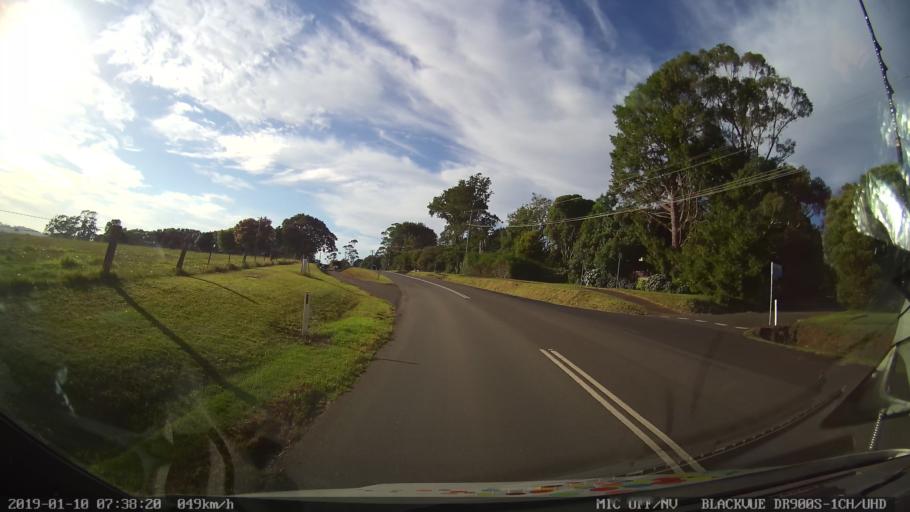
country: AU
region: New South Wales
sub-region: Bellingen
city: Dorrigo
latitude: -30.3481
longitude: 152.7149
